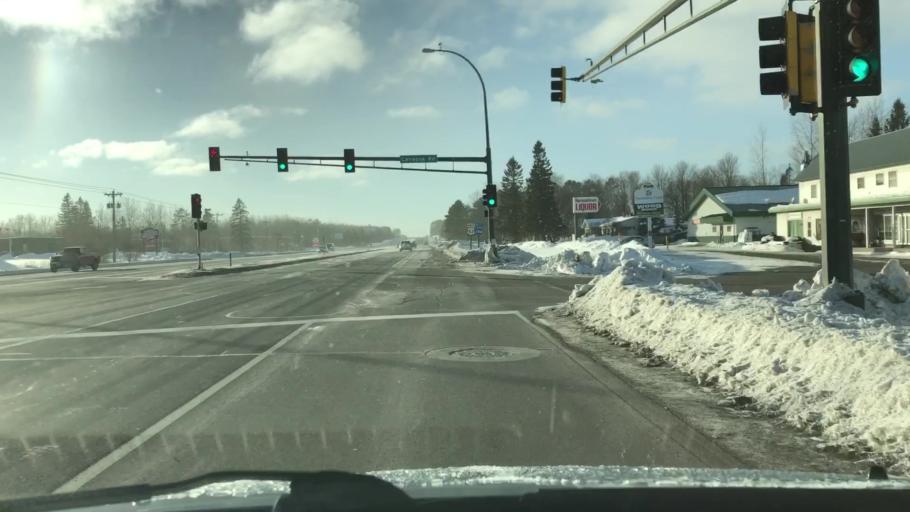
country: US
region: Minnesota
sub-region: Saint Louis County
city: Hermantown
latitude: 46.8368
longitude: -92.2167
